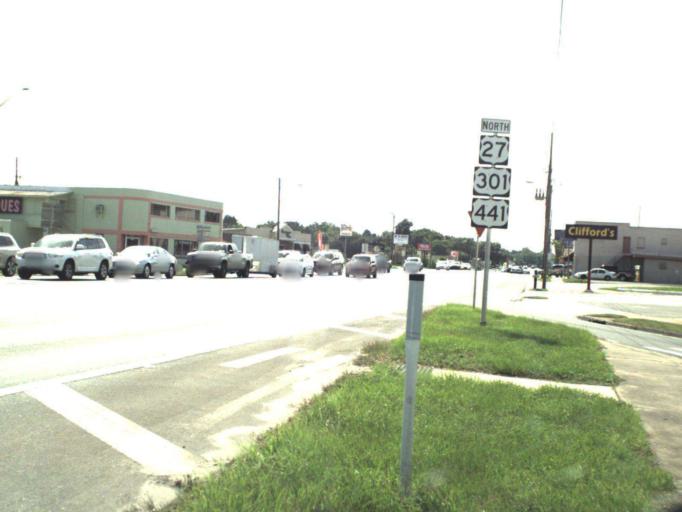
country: US
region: Florida
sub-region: Marion County
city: Belleview
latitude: 29.0590
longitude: -82.0530
